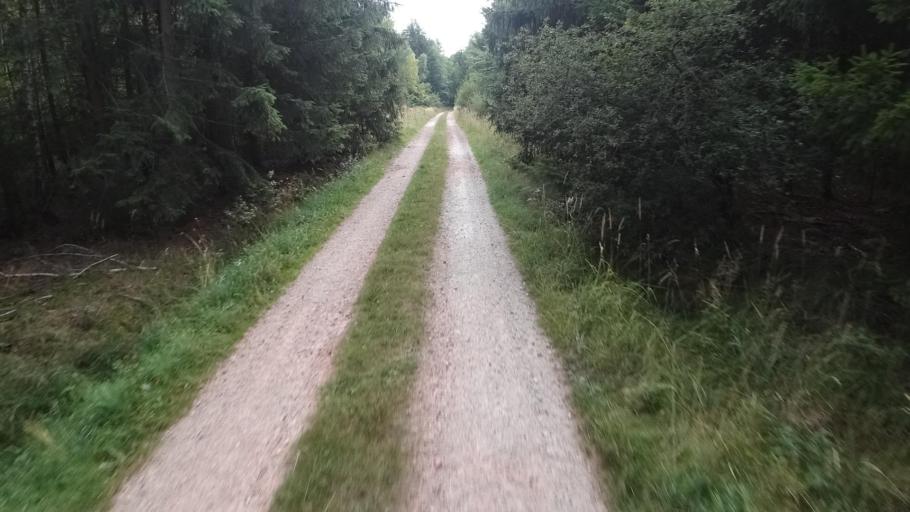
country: DE
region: Rheinland-Pfalz
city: Dichtelbach
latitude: 50.0131
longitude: 7.7128
